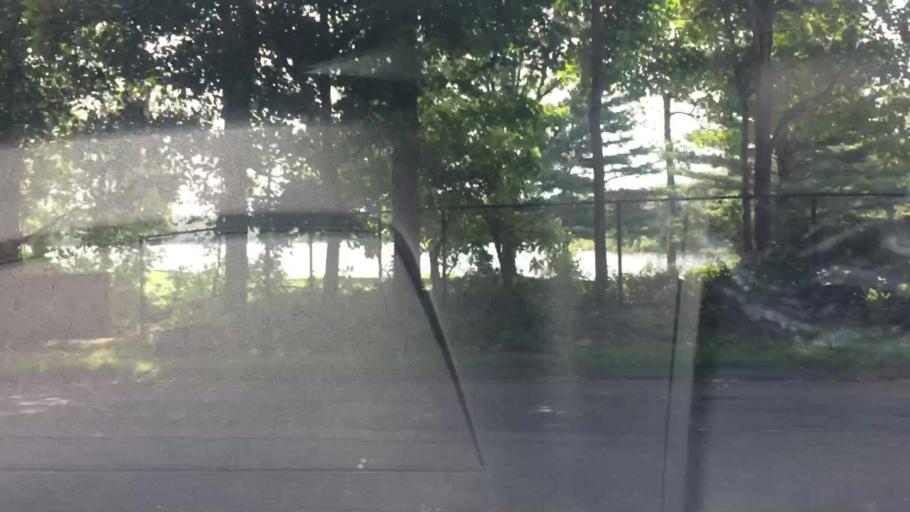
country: US
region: Connecticut
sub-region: Fairfield County
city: Danbury
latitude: 41.4132
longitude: -73.5106
